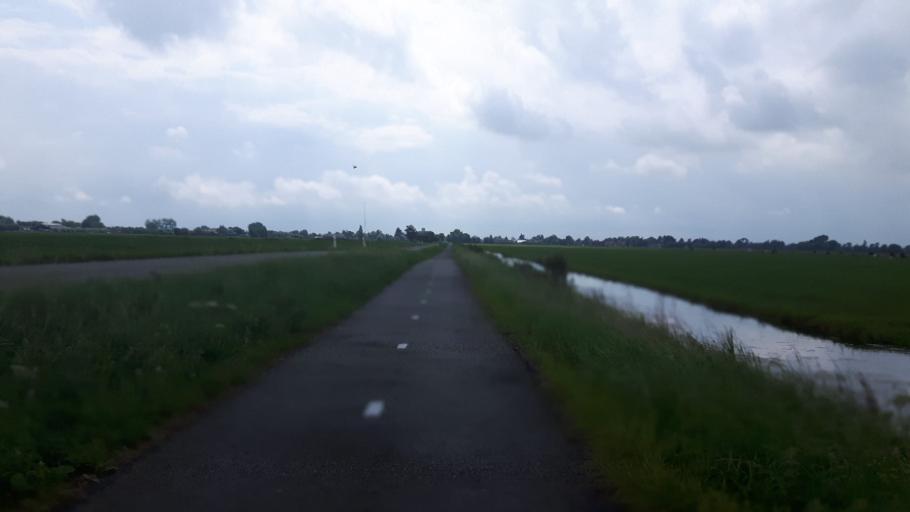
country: NL
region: Utrecht
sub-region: Gemeente Oudewater
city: Oudewater
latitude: 52.0047
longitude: 4.8974
